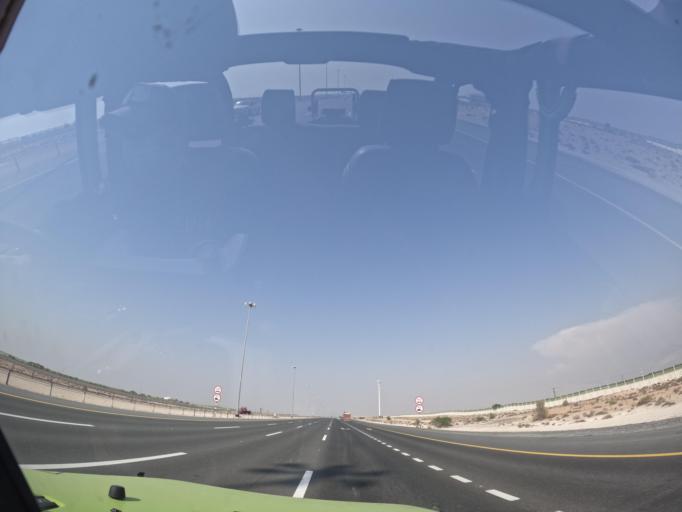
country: AE
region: Abu Dhabi
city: Abu Dhabi
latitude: 24.6305
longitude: 54.7768
